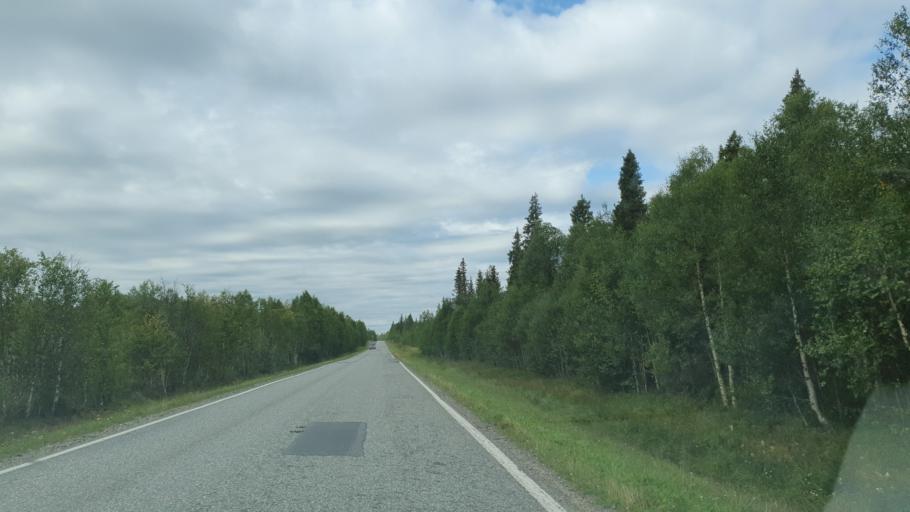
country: FI
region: Lapland
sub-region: Tunturi-Lappi
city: Kittilae
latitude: 67.6156
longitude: 25.3621
